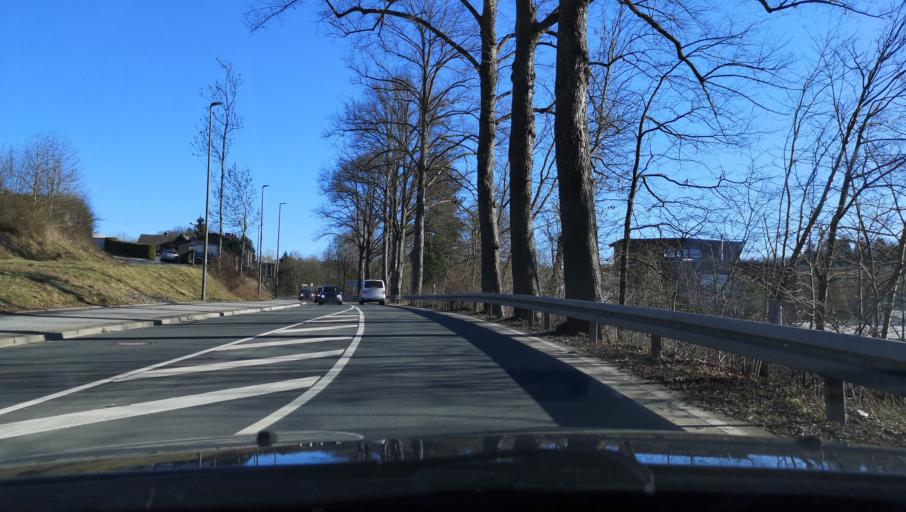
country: DE
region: North Rhine-Westphalia
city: Wipperfurth
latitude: 51.1209
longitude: 7.4128
